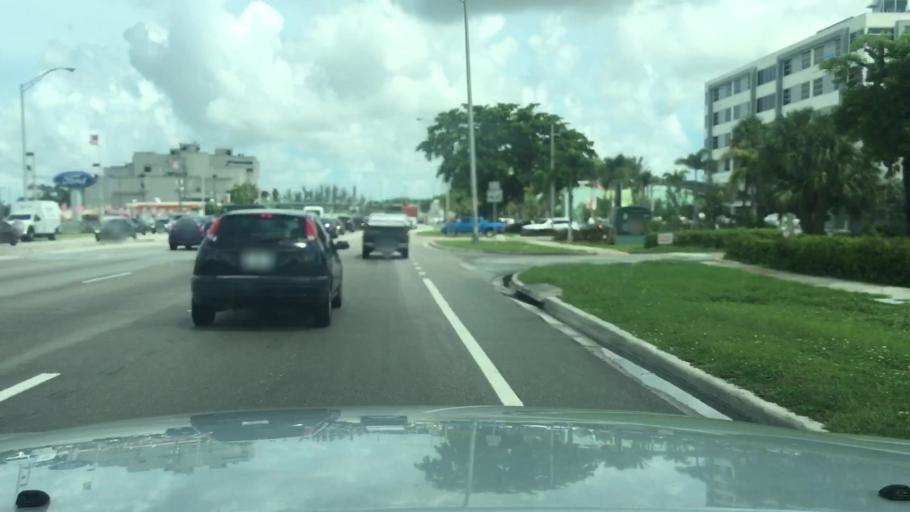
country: US
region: Florida
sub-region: Miami-Dade County
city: Virginia Gardens
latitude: 25.8092
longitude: -80.3161
